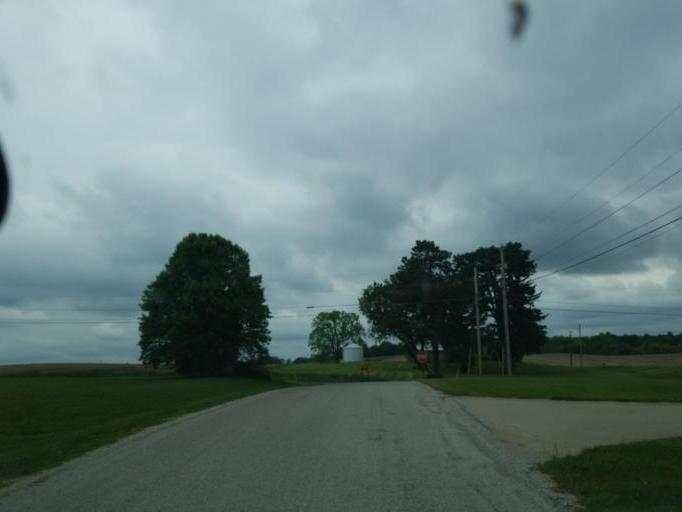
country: US
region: Ohio
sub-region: Richland County
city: Lexington
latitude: 40.6655
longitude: -82.6233
